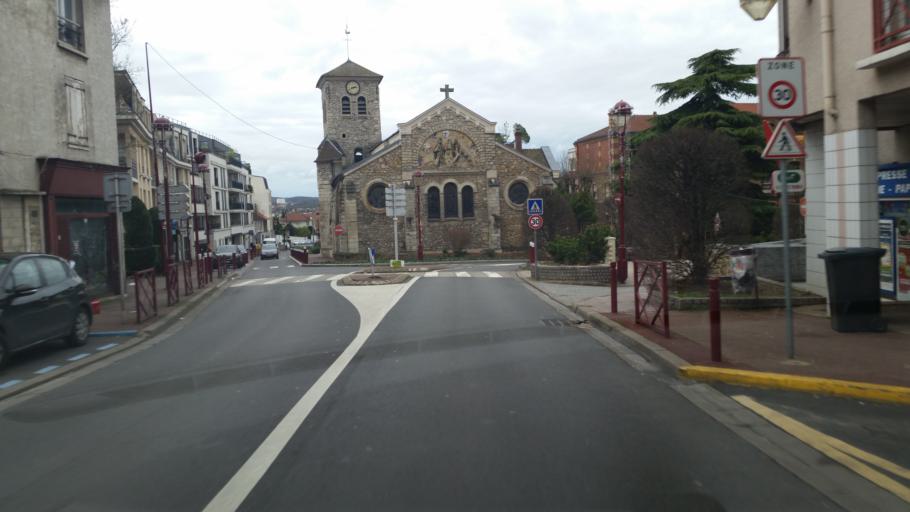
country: FR
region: Ile-de-France
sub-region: Departement du Val-de-Marne
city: Fresnes
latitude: 48.7544
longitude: 2.3231
